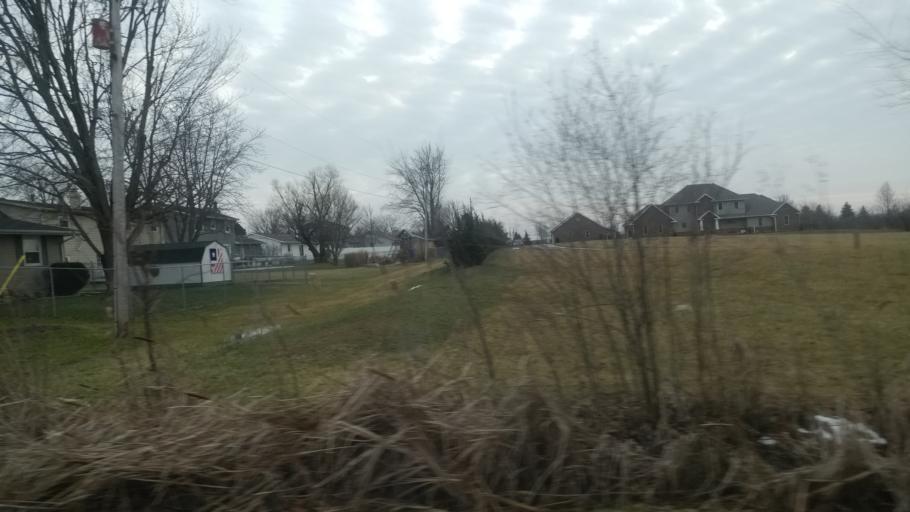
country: US
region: Ohio
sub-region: Hancock County
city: Findlay
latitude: 41.0731
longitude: -83.6701
